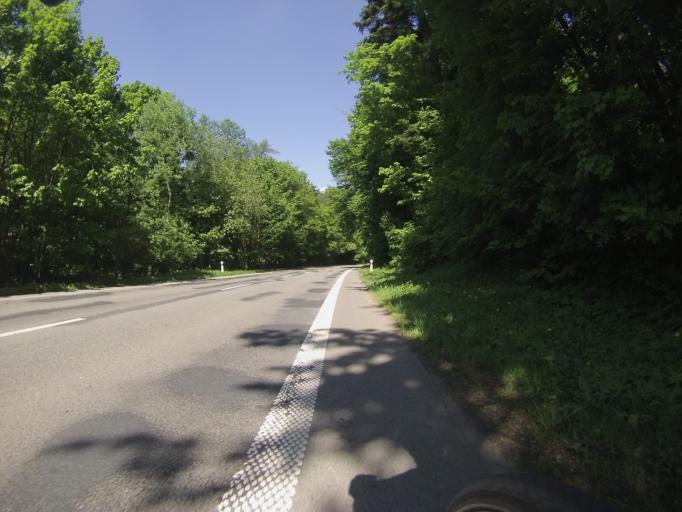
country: CZ
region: South Moravian
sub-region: Okres Blansko
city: Adamov
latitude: 49.3283
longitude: 16.6340
